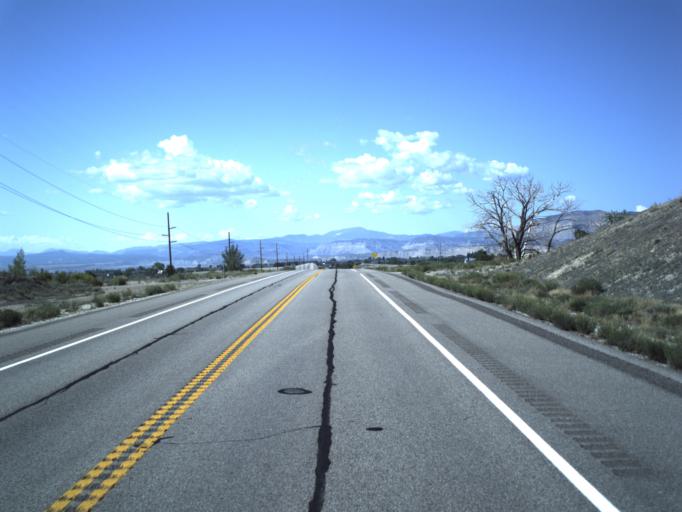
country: US
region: Utah
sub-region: Emery County
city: Ferron
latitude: 38.9343
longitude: -111.2294
